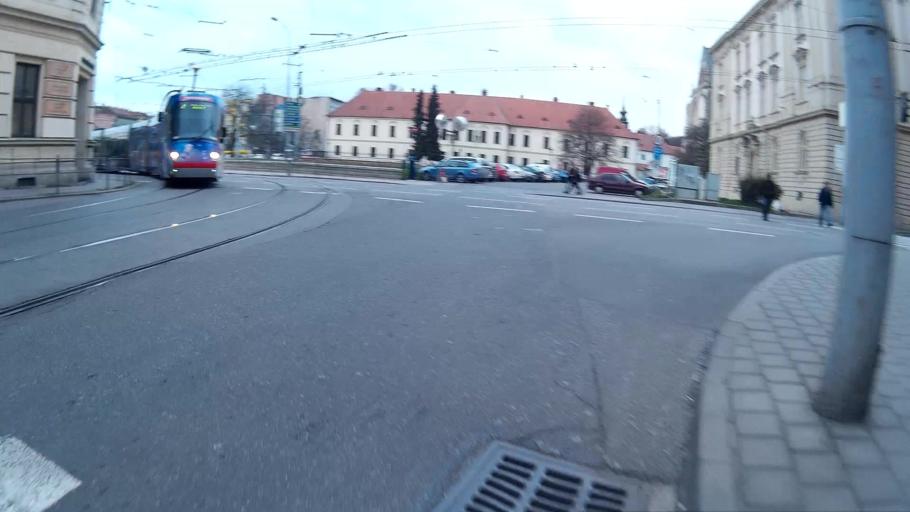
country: CZ
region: South Moravian
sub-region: Mesto Brno
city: Brno
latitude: 49.1916
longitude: 16.5960
